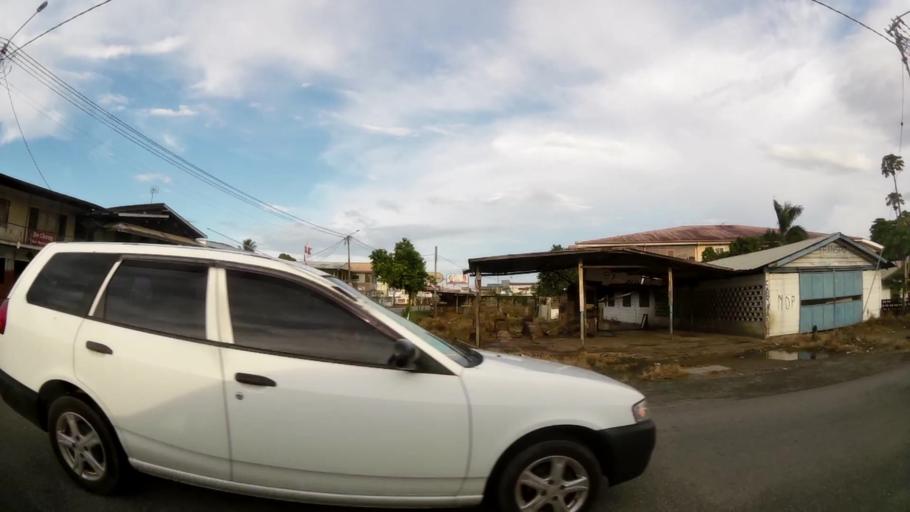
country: SR
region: Paramaribo
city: Paramaribo
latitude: 5.8392
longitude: -55.1817
